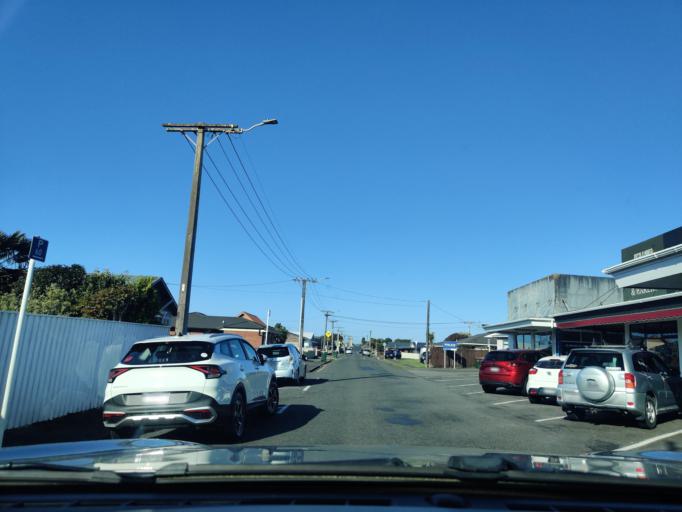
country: NZ
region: Taranaki
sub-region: New Plymouth District
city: New Plymouth
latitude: -39.0492
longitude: 174.1025
